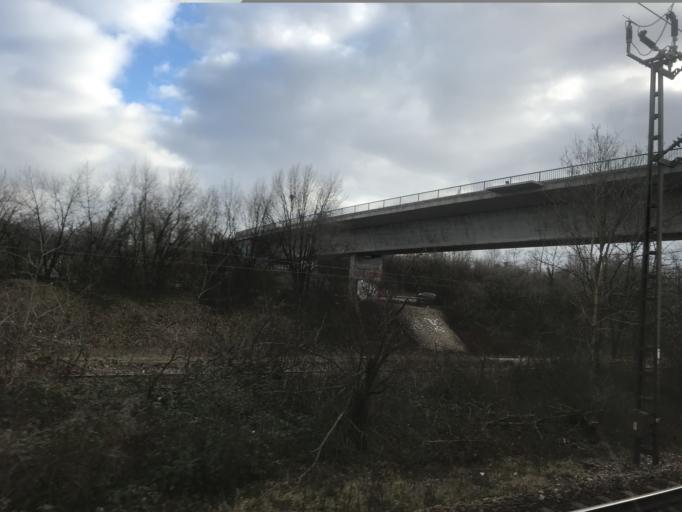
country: DE
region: Baden-Wuerttemberg
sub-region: Freiburg Region
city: Weil am Rhein
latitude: 47.6052
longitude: 7.6158
